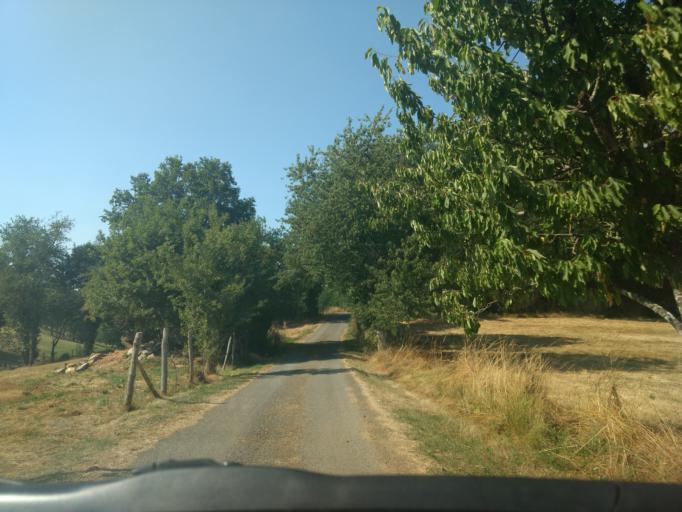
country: FR
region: Midi-Pyrenees
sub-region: Departement de l'Aveyron
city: Livinhac-le-Haut
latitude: 44.6092
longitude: 2.1590
